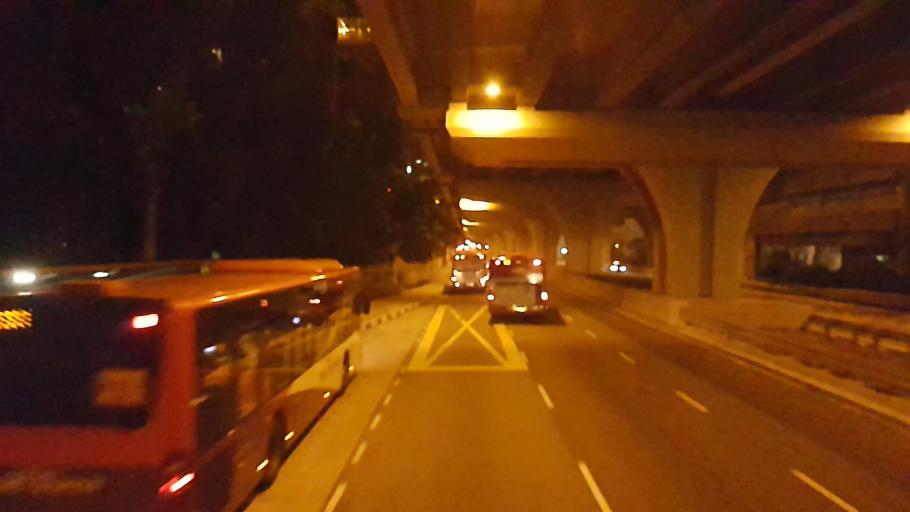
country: SG
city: Singapore
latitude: 1.2725
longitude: 103.8368
